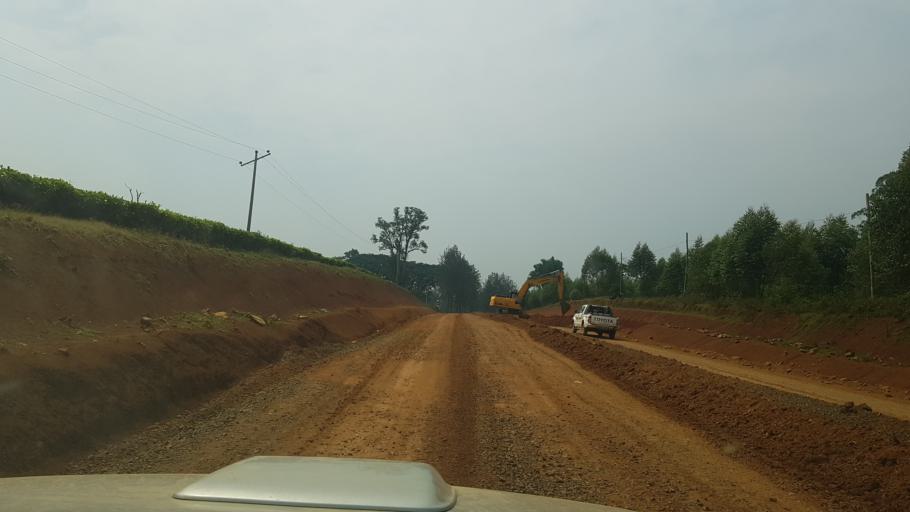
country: ET
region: Oromiya
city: Gore
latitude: 7.8472
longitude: 35.4766
